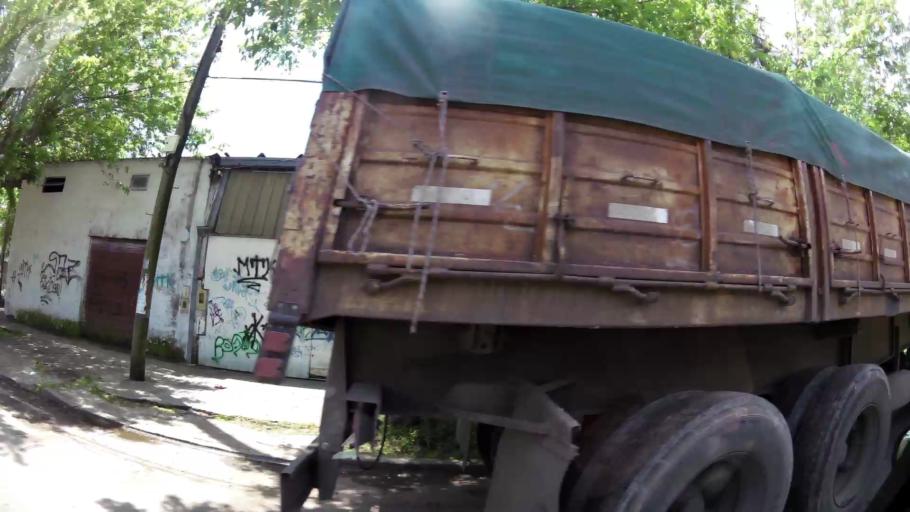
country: AR
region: Buenos Aires
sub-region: Partido de Quilmes
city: Quilmes
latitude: -34.7832
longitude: -58.2643
